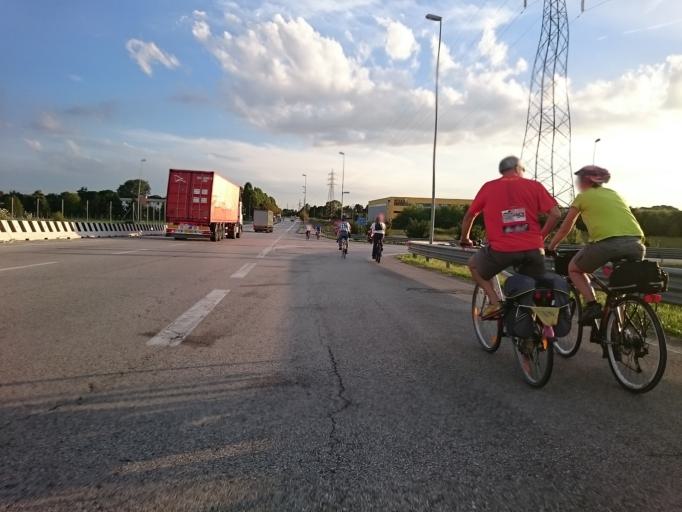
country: IT
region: Veneto
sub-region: Provincia di Padova
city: Ponte San Nicolo
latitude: 45.3816
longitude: 11.9388
